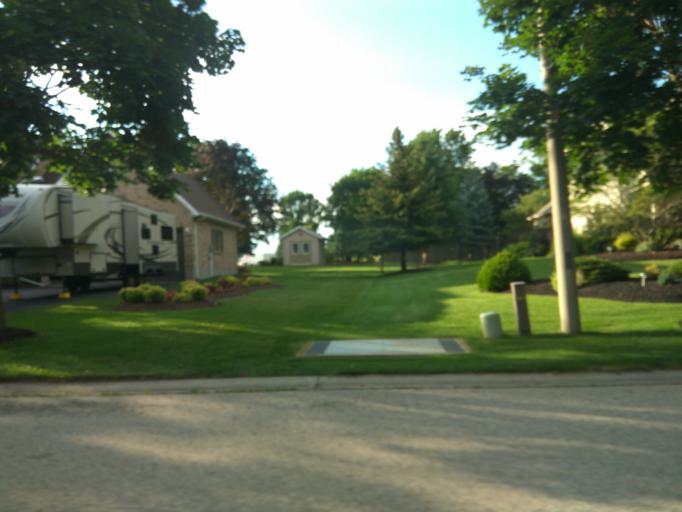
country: CA
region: Ontario
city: Kitchener
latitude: 43.3731
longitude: -80.6965
